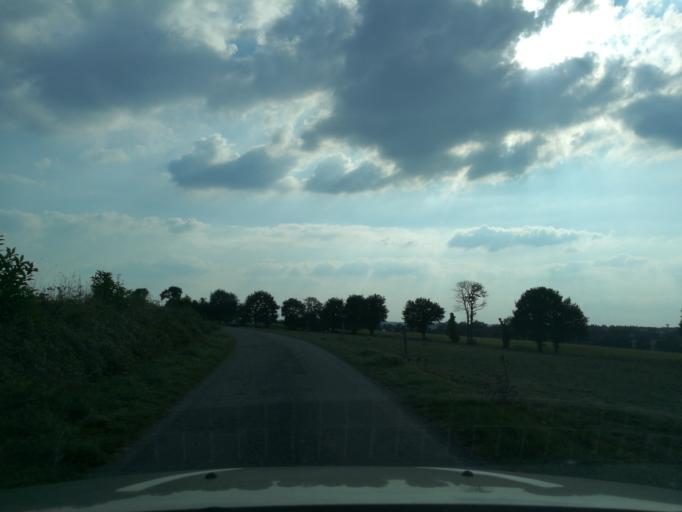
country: FR
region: Brittany
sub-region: Departement d'Ille-et-Vilaine
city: Montauban-de-Bretagne
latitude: 48.1949
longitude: -1.9961
